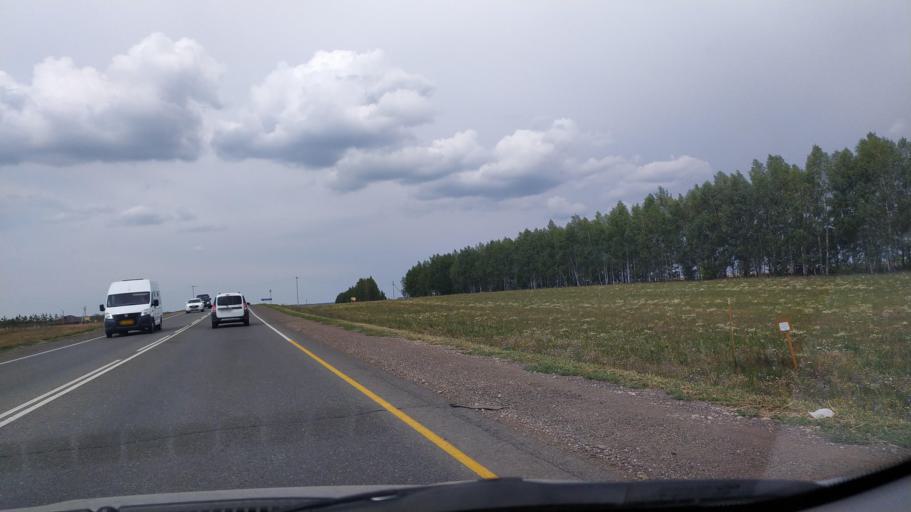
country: RU
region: Tatarstan
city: Al'met'yevsk
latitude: 54.9013
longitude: 52.2162
